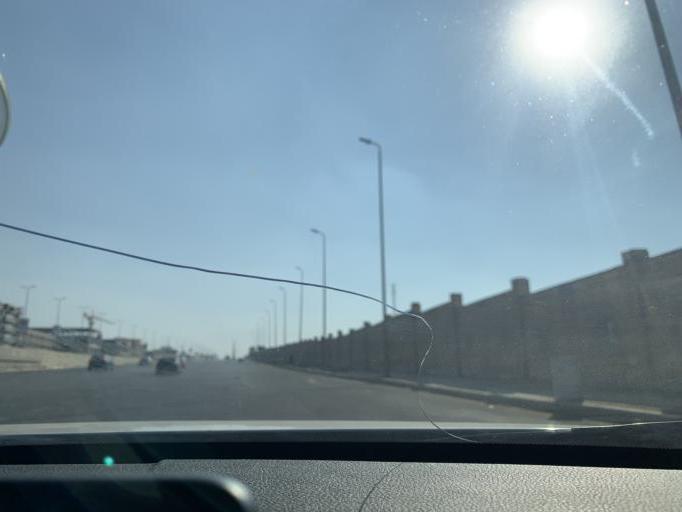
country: EG
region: Muhafazat al Qalyubiyah
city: Al Khankah
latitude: 30.0238
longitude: 31.4746
